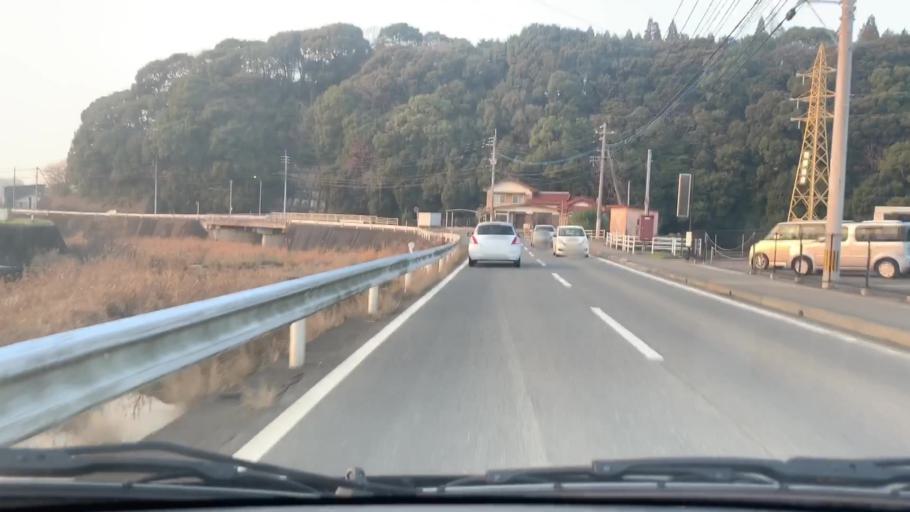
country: JP
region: Saga Prefecture
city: Imaricho-ko
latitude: 33.2711
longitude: 129.8950
